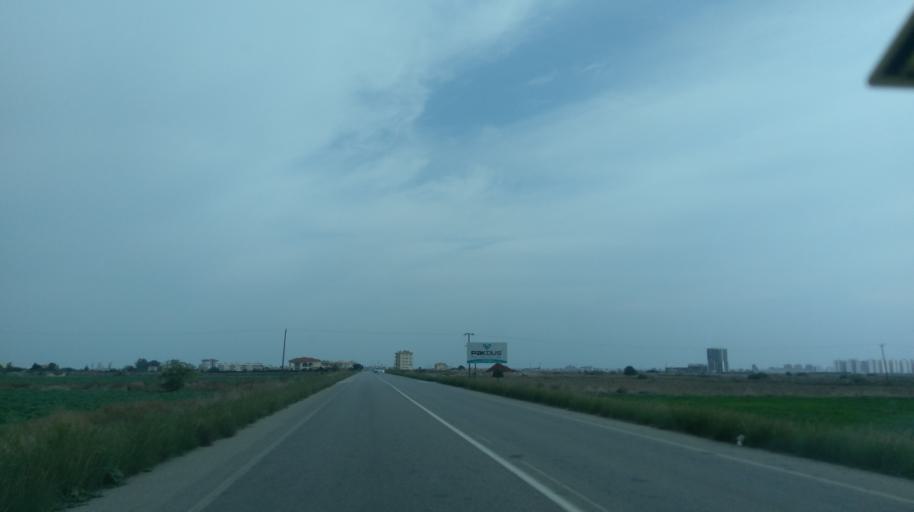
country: CY
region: Ammochostos
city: Trikomo
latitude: 35.2799
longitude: 33.8838
